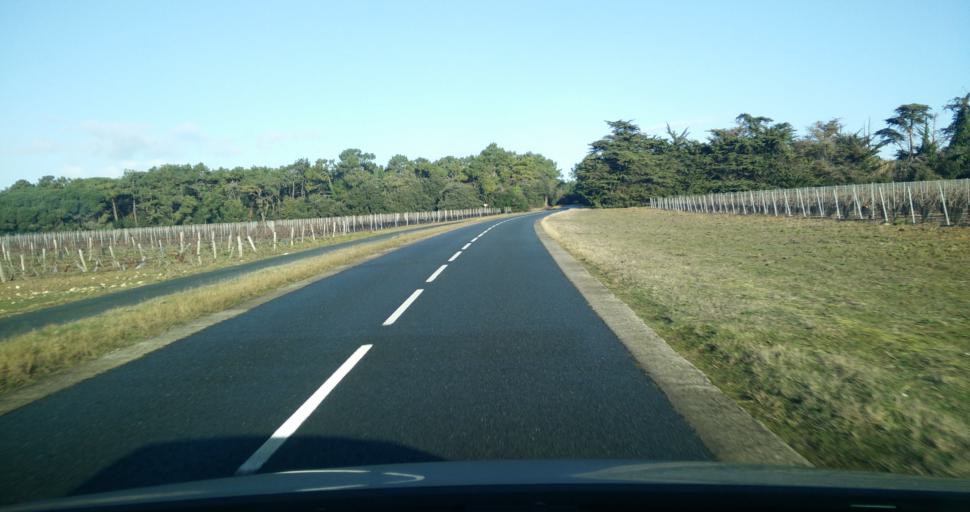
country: FR
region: Poitou-Charentes
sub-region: Departement de la Charente-Maritime
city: Sainte-Marie-de-Re
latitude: 46.1666
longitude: -1.3244
